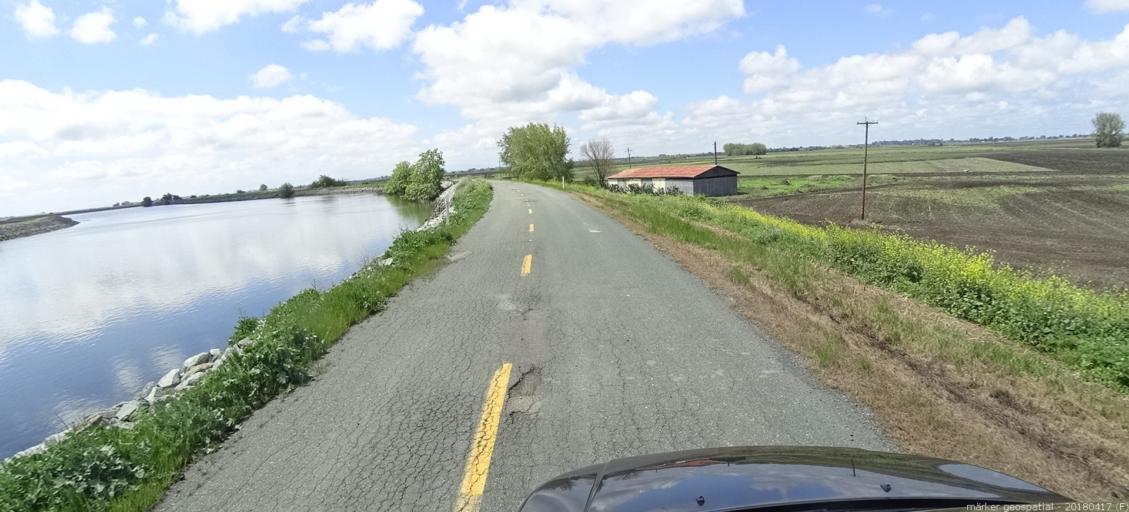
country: US
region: California
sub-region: Sacramento County
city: Walnut Grove
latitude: 38.1704
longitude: -121.5286
